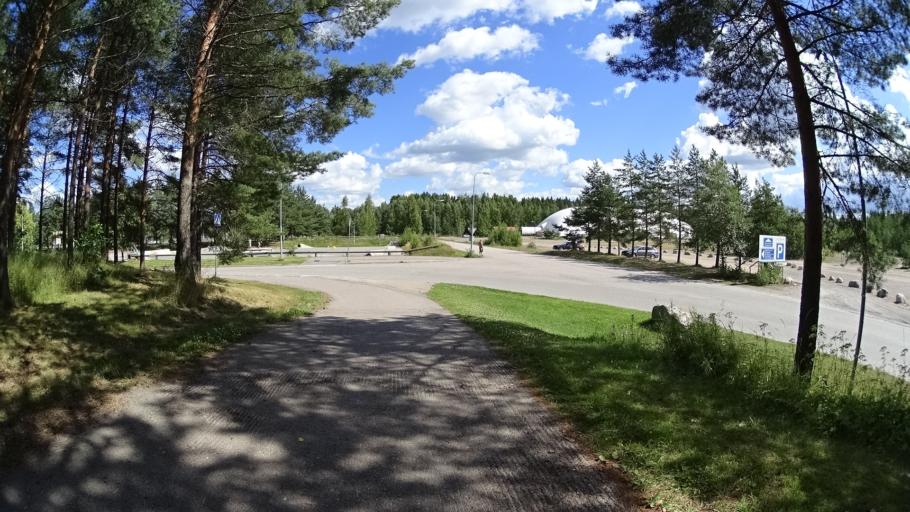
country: FI
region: Uusimaa
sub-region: Helsinki
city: Tuusula
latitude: 60.3908
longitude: 25.0311
